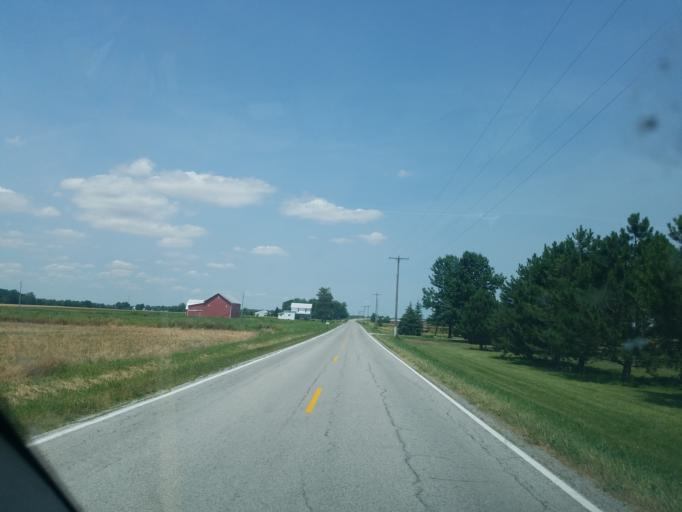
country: US
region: Ohio
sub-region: Wyandot County
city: Carey
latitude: 40.9611
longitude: -83.4860
